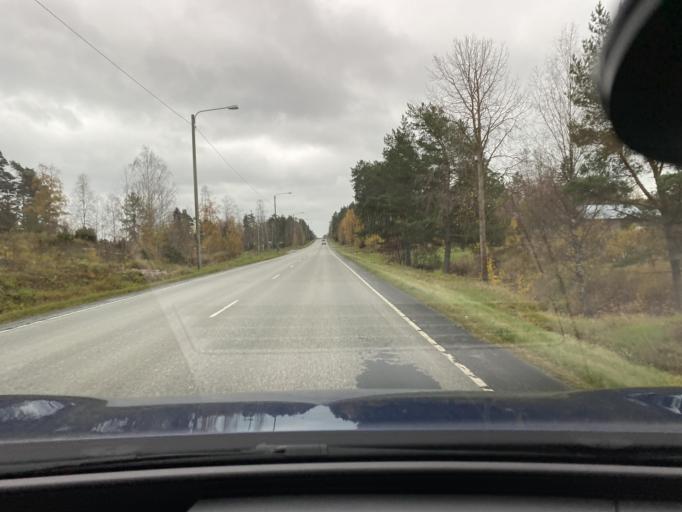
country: FI
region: Varsinais-Suomi
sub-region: Vakka-Suomi
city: Laitila
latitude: 60.9712
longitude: 21.5936
